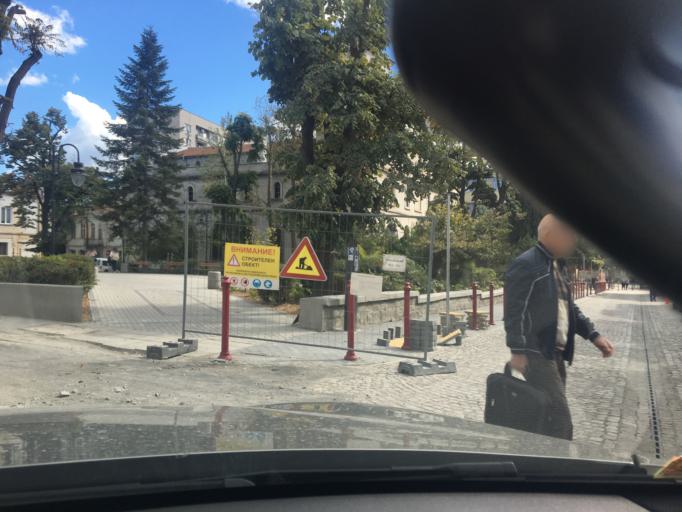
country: BG
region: Burgas
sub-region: Obshtina Burgas
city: Burgas
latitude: 42.4928
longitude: 27.4747
